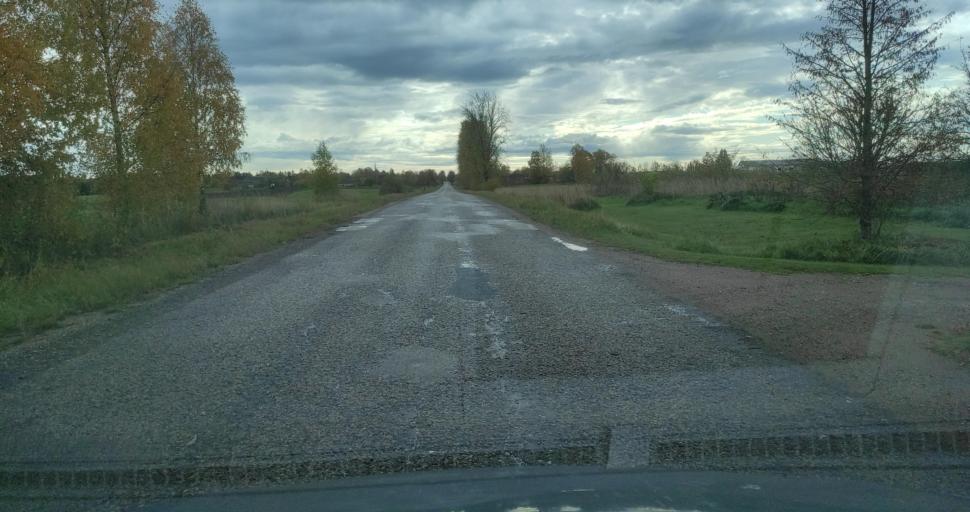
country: LV
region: Vainode
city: Vainode
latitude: 56.5756
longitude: 21.8892
